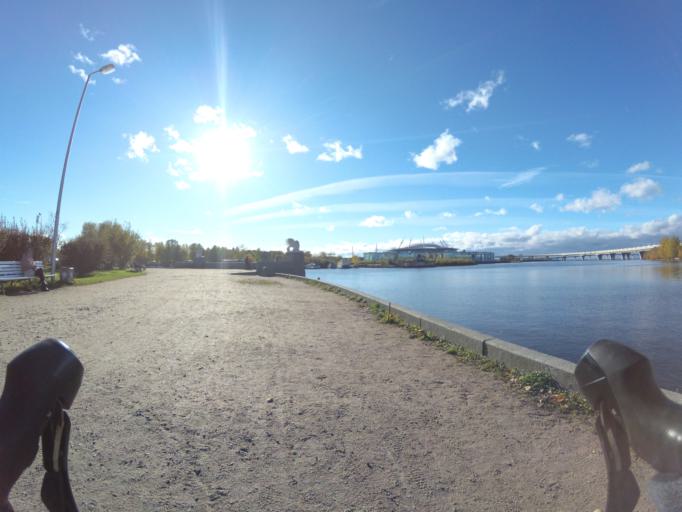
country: RU
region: St.-Petersburg
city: Staraya Derevnya
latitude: 59.9804
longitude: 30.2367
